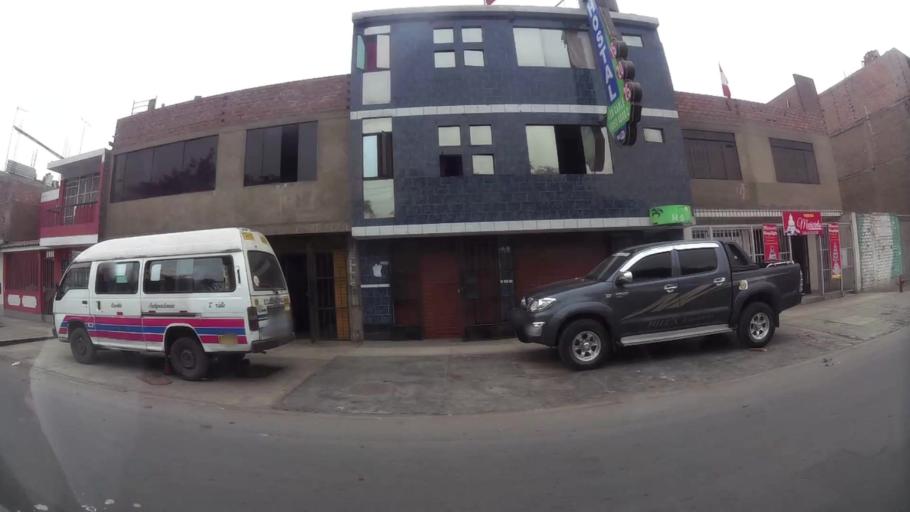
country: PE
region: Lima
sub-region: Lima
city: Independencia
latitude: -11.9734
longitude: -77.0819
